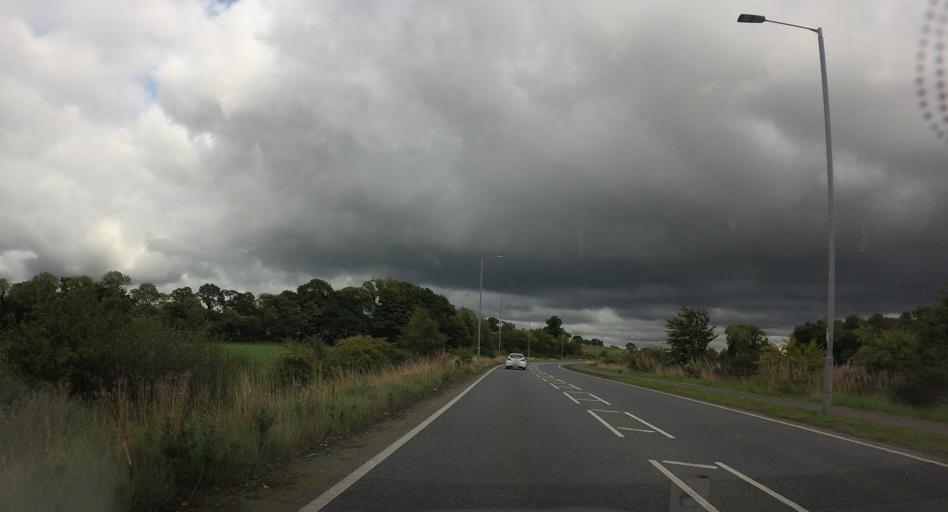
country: GB
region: Scotland
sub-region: Clackmannanshire
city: Alloa
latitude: 56.1175
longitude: -3.7730
